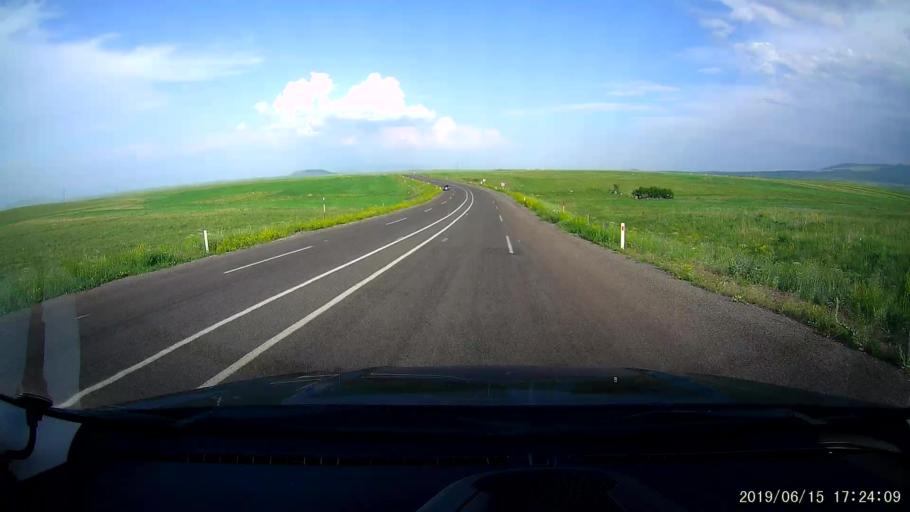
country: TR
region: Kars
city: Basgedikler
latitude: 40.6154
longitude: 43.3772
